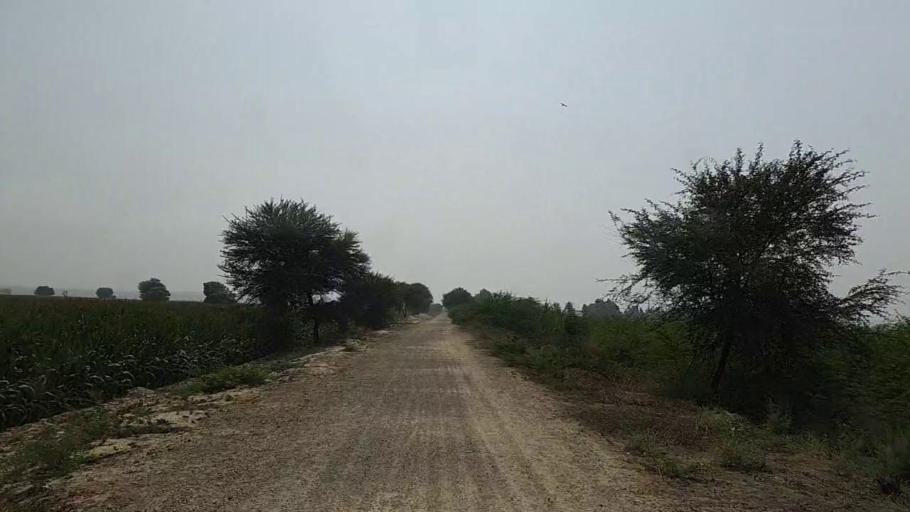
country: PK
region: Sindh
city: Naukot
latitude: 24.8176
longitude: 69.3994
